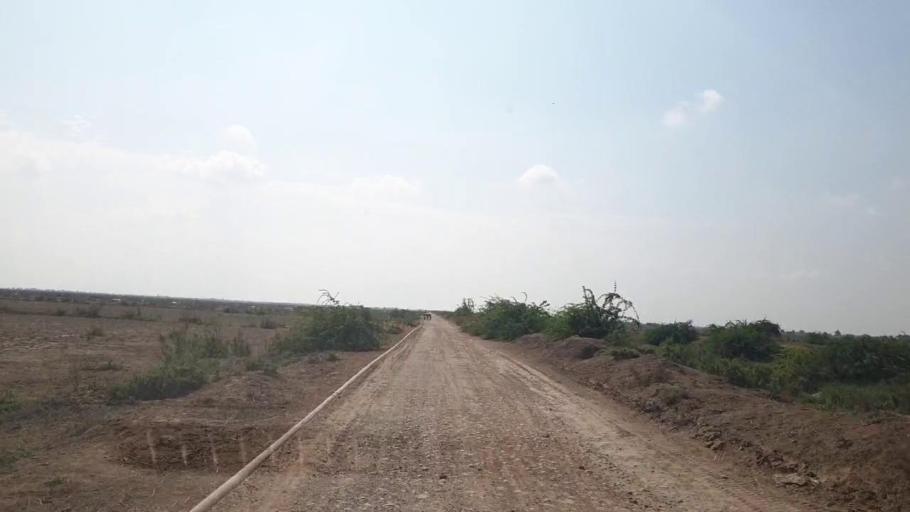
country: PK
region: Sindh
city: Badin
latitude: 24.5109
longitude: 68.6081
